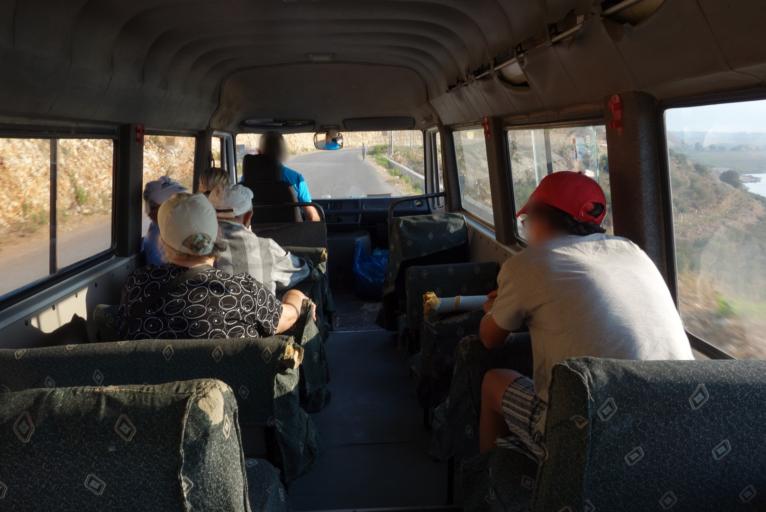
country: AL
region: Vlore
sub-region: Rrethi i Sarandes
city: Sarande
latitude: 39.8074
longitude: 20.0103
